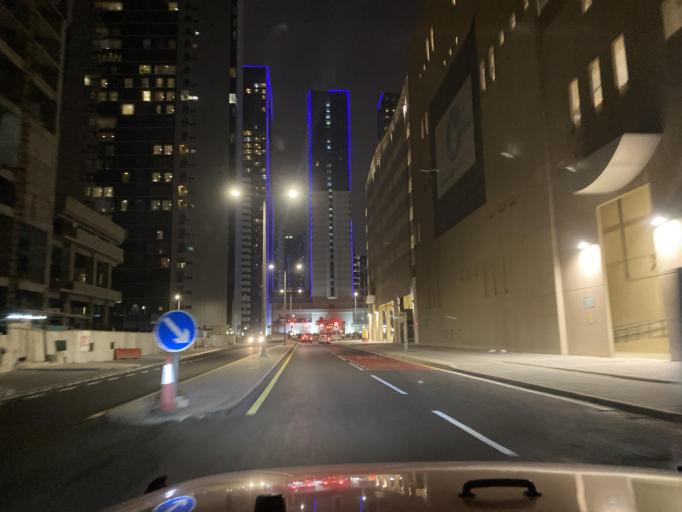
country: QA
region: Baladiyat ad Dawhah
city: Doha
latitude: 25.3214
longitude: 51.5220
